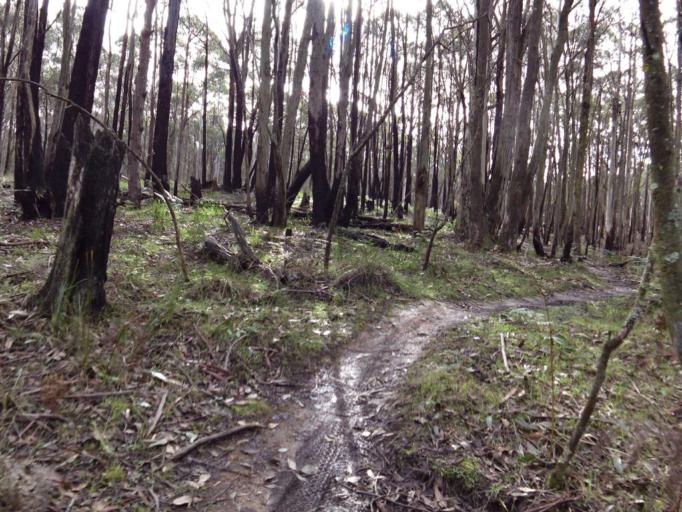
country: AU
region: Victoria
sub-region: Moorabool
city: Bacchus Marsh
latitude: -37.4124
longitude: 144.4924
